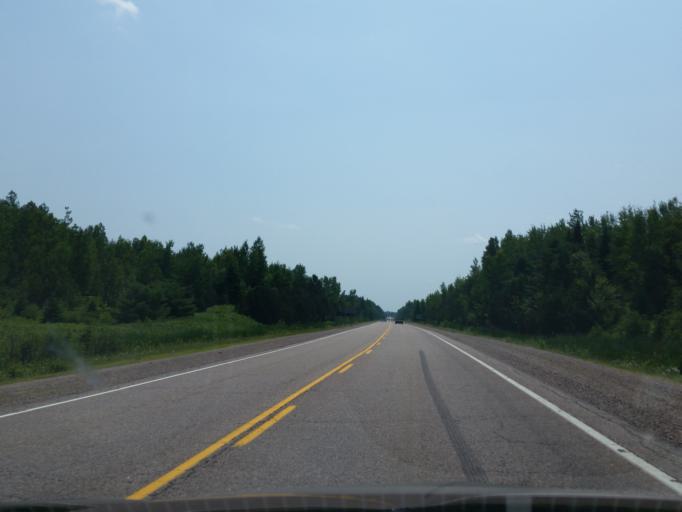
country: CA
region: Ontario
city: Petawawa
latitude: 45.8697
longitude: -77.2969
